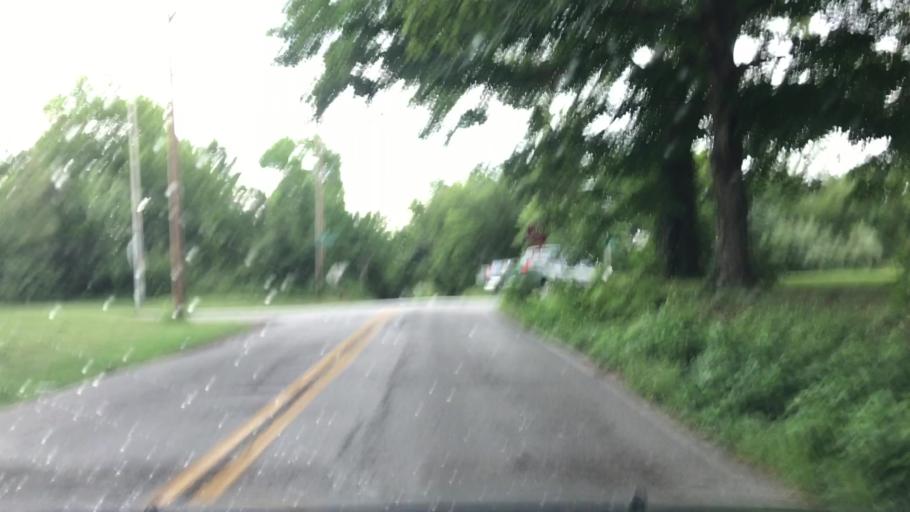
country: US
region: Missouri
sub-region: Jackson County
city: Grandview
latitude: 38.9297
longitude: -94.4862
